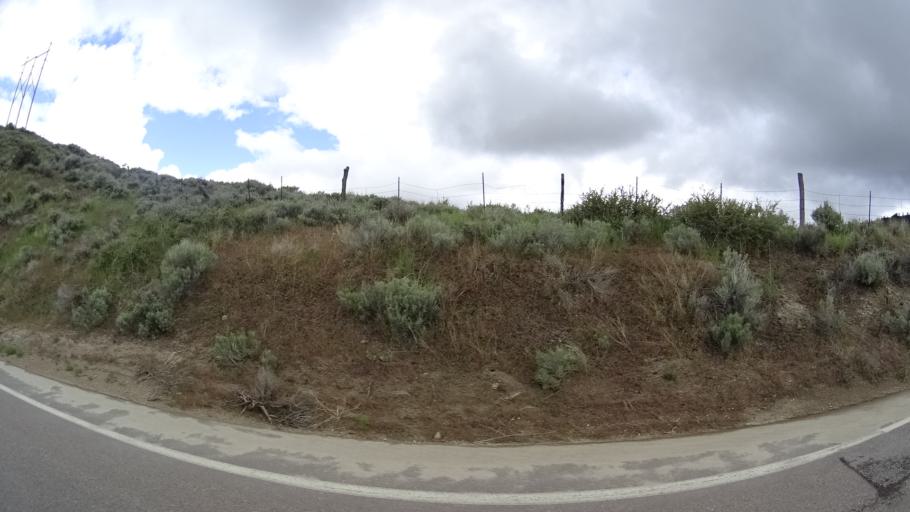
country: US
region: Idaho
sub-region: Ada County
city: Boise
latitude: 43.7224
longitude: -116.1609
